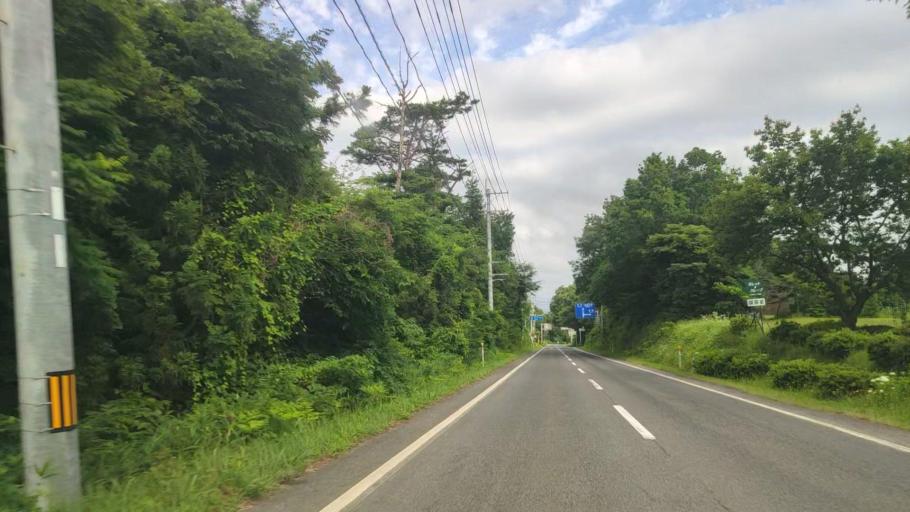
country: JP
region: Tottori
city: Yonago
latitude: 35.4113
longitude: 133.4726
